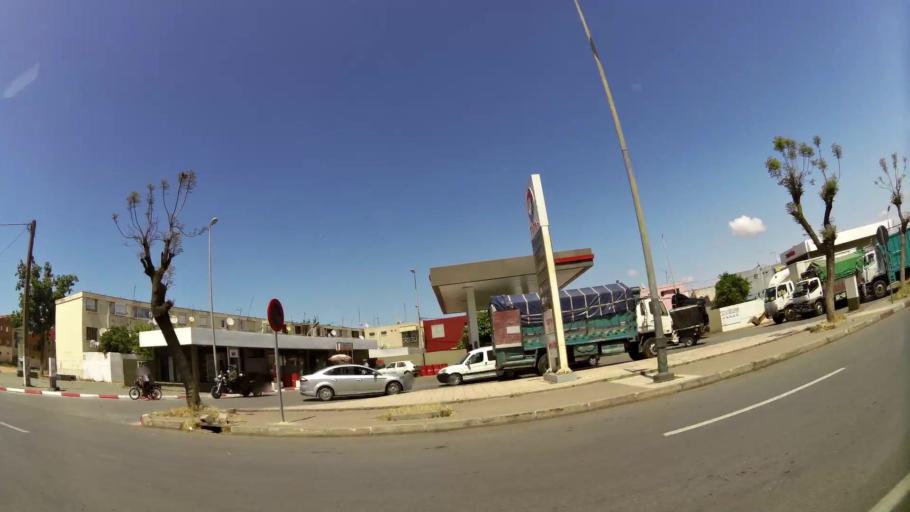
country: MA
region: Gharb-Chrarda-Beni Hssen
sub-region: Kenitra Province
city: Kenitra
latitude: 34.2487
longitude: -6.5549
